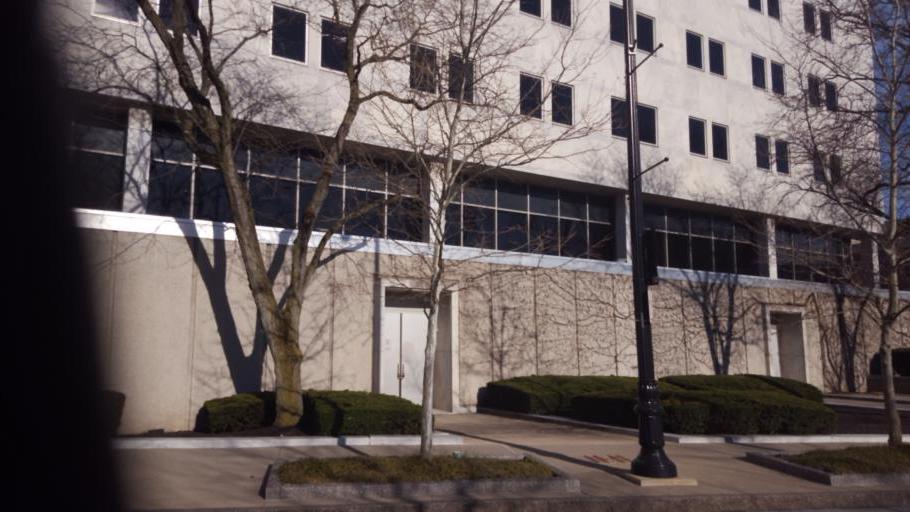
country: US
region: Ohio
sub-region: Franklin County
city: Columbus
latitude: 39.9590
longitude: -83.0028
